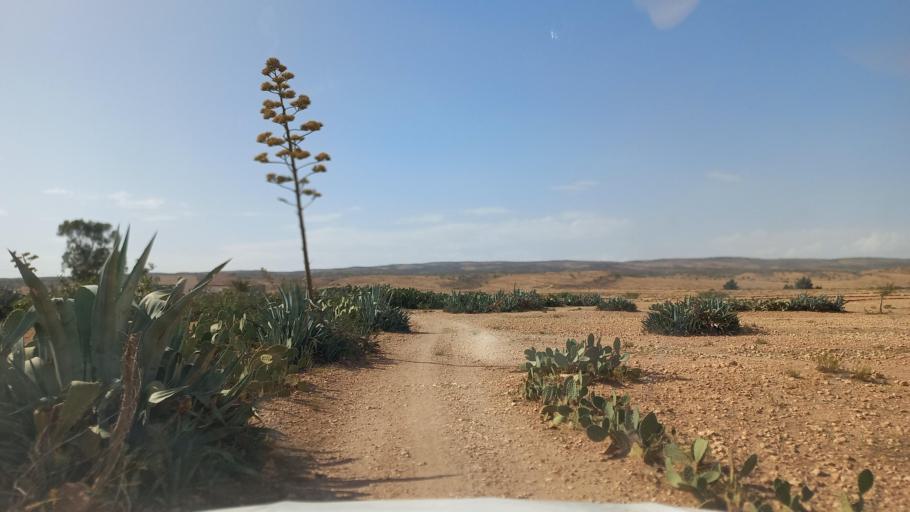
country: TN
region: Al Qasrayn
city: Kasserine
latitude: 35.2871
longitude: 8.9376
